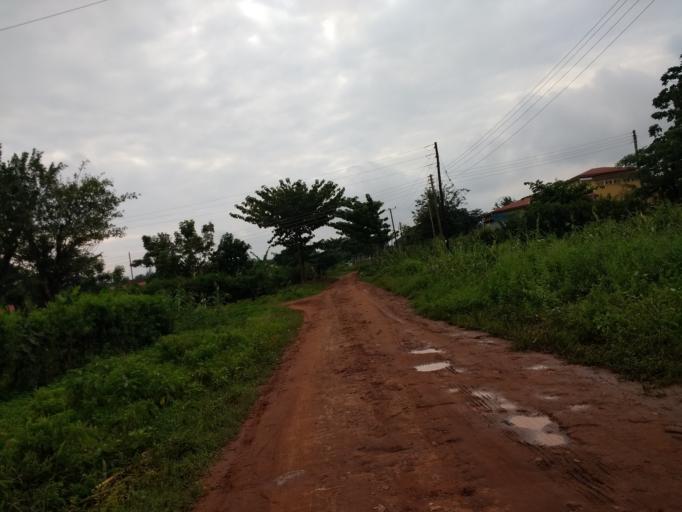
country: UG
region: Eastern Region
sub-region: Mbale District
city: Mbale
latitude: 1.0702
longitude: 34.1667
